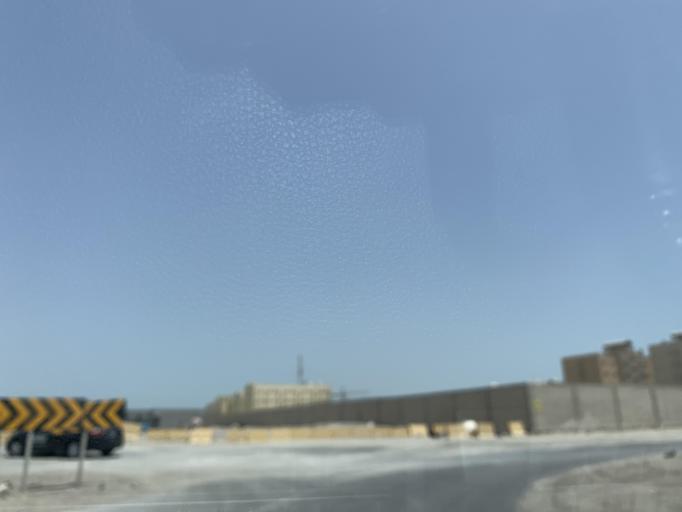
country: BH
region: Northern
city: Sitrah
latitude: 26.1428
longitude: 50.5948
